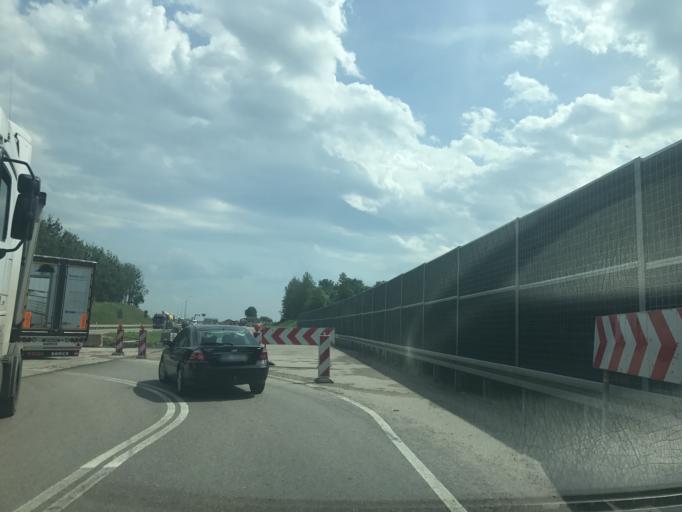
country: PL
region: Warmian-Masurian Voivodeship
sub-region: Powiat ostrodzki
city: Ostroda
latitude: 53.6910
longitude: 19.9888
